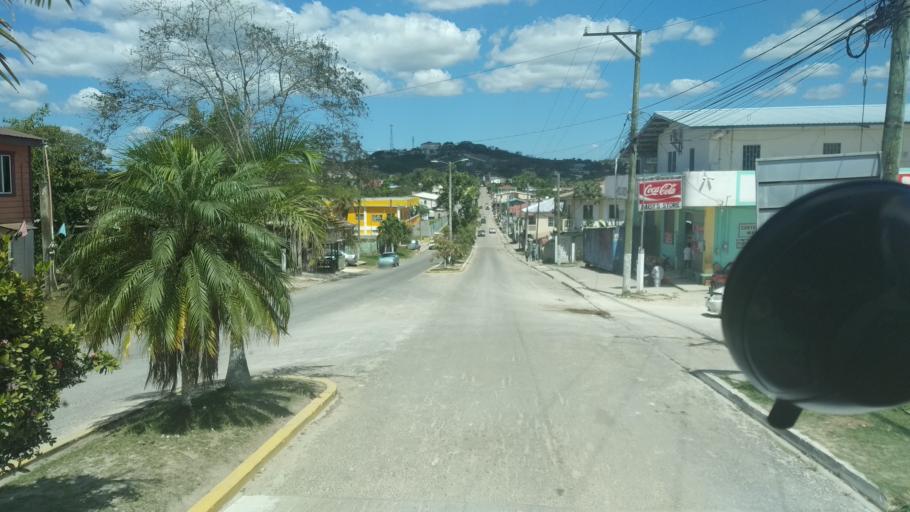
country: BZ
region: Cayo
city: Benque Viejo del Carmen
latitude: 17.0708
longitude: -89.1392
